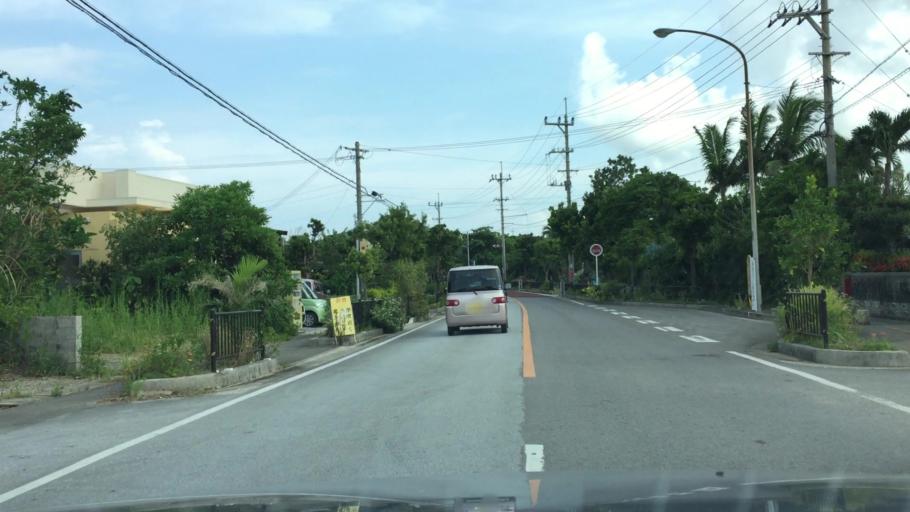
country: JP
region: Okinawa
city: Ishigaki
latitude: 24.4546
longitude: 124.2485
